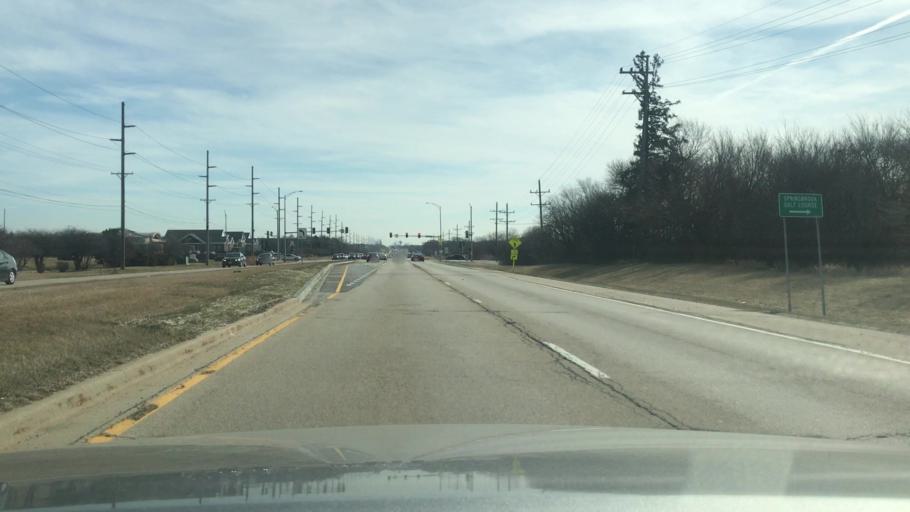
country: US
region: Illinois
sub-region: DuPage County
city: Naperville
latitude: 41.7473
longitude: -88.1890
